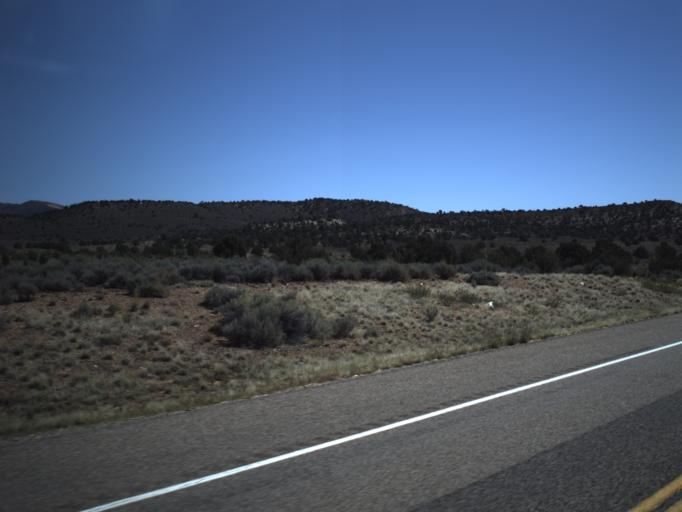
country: US
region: Utah
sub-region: Washington County
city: Ivins
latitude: 37.2878
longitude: -113.6580
